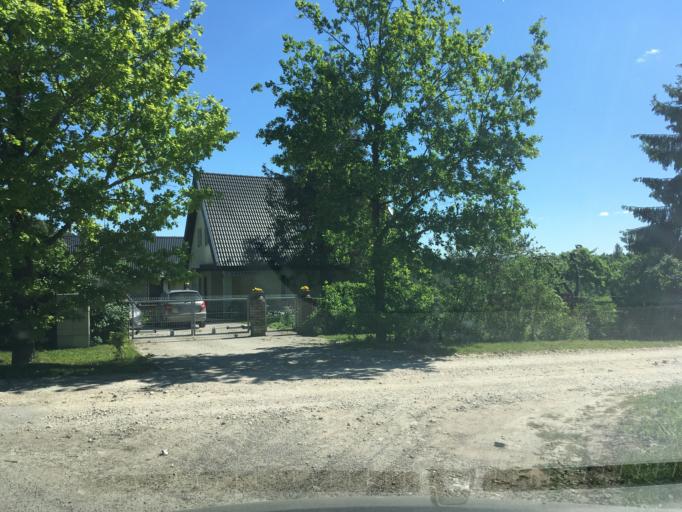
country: EE
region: Harju
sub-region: Rae vald
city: Vaida
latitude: 59.1574
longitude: 25.1261
